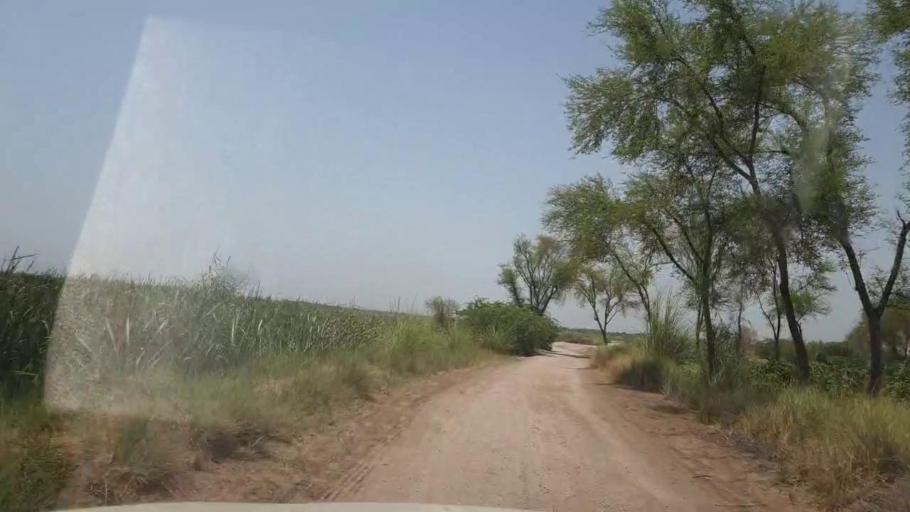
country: PK
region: Sindh
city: Bozdar
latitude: 27.1351
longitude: 68.6183
